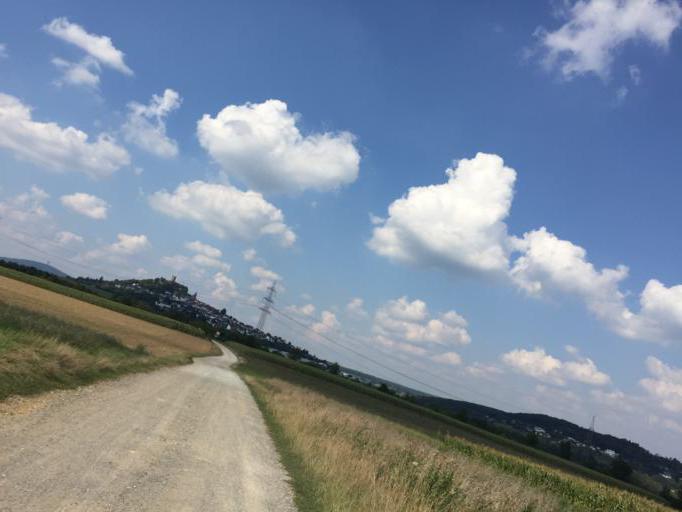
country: DE
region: Hesse
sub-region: Regierungsbezirk Giessen
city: Heuchelheim
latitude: 50.6028
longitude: 8.6462
